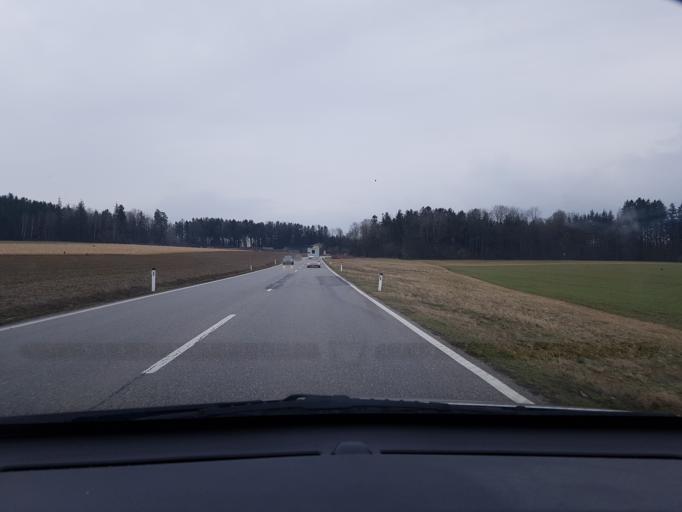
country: AT
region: Upper Austria
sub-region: Steyr Stadt
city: Steyr
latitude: 48.0662
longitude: 14.3865
